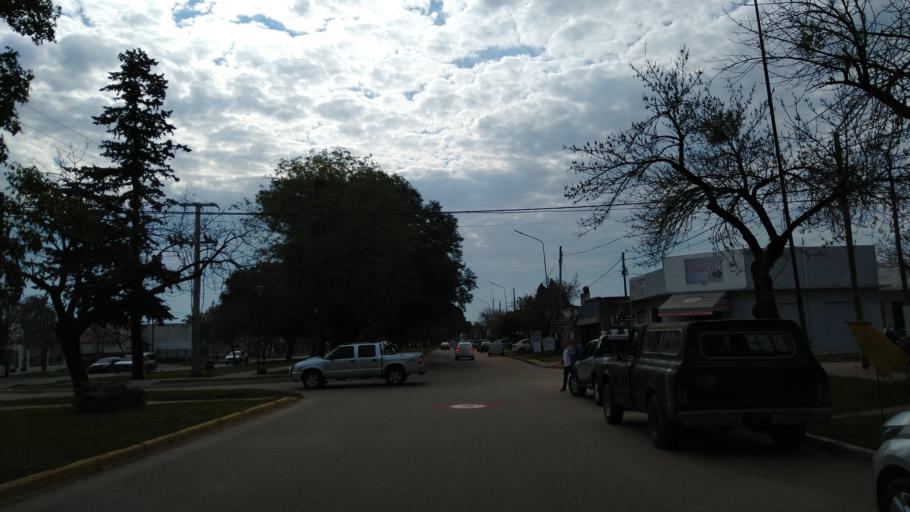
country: AR
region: Entre Rios
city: Chajari
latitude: -30.7612
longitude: -57.9914
